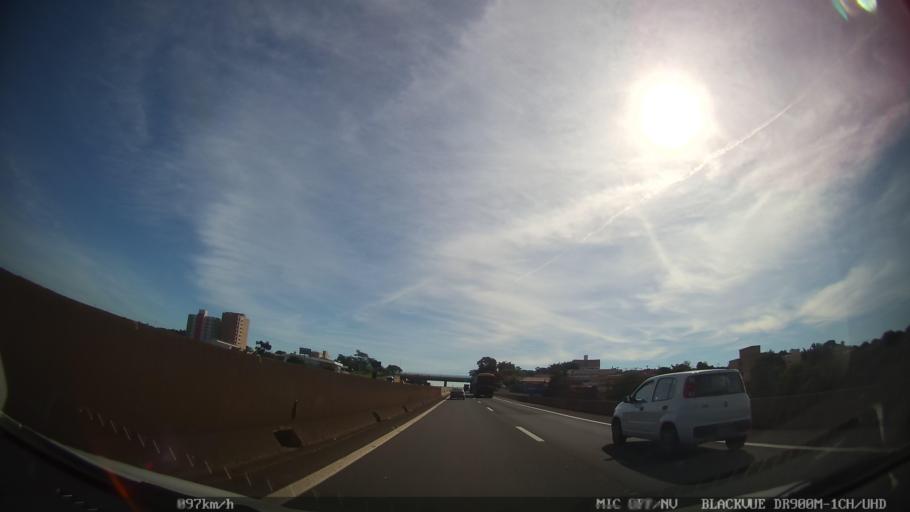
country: BR
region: Sao Paulo
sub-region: Araras
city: Araras
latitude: -22.3601
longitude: -47.3946
